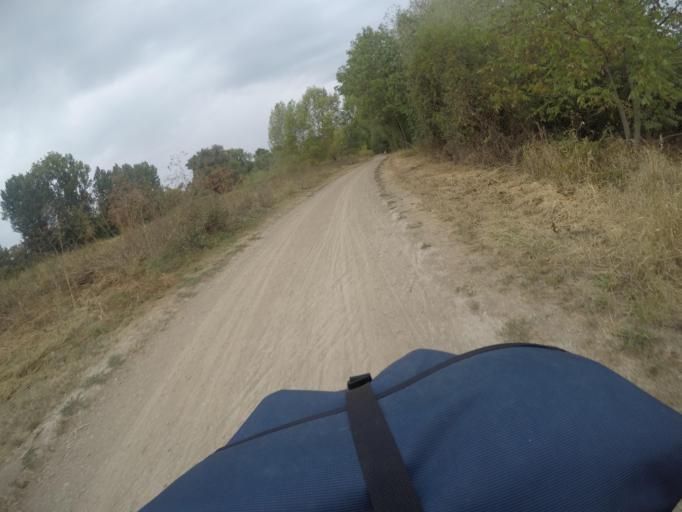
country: DE
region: Hesse
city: Geisenheim
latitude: 49.9704
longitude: 7.9528
